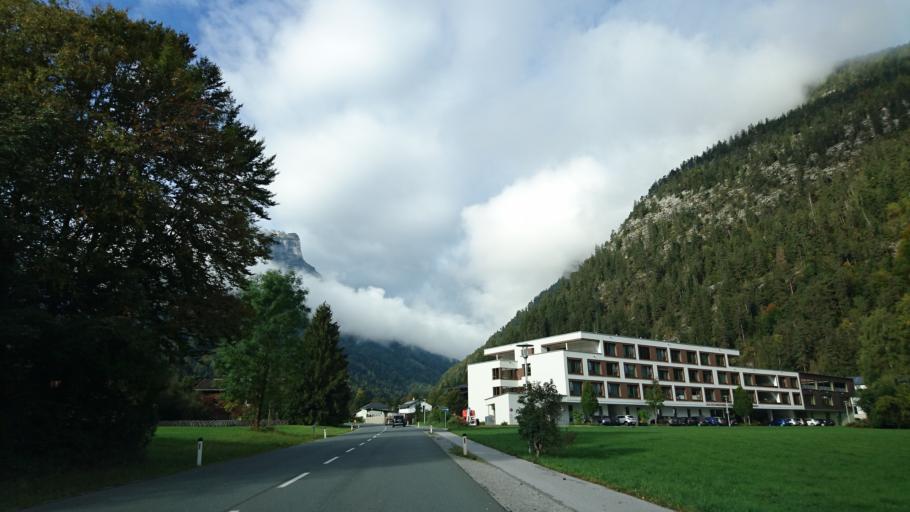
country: AT
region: Salzburg
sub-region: Politischer Bezirk Zell am See
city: Lofer
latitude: 47.5830
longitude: 12.6914
